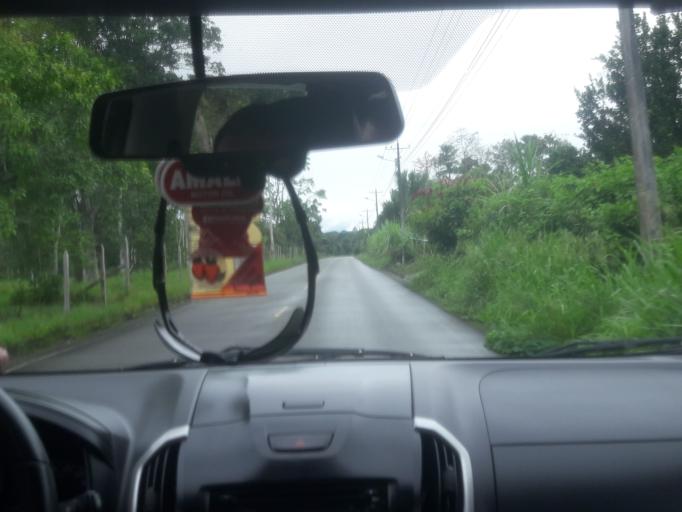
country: EC
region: Napo
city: Tena
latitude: -1.0438
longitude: -77.7043
